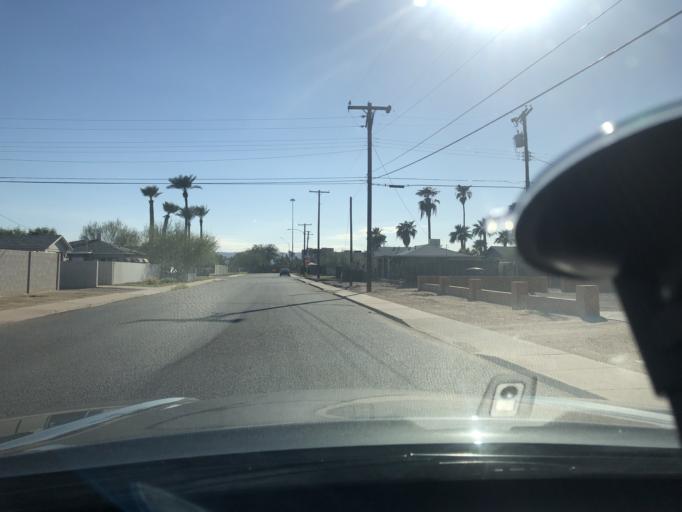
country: US
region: Arizona
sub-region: Maricopa County
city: Phoenix
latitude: 33.4646
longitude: -112.0412
